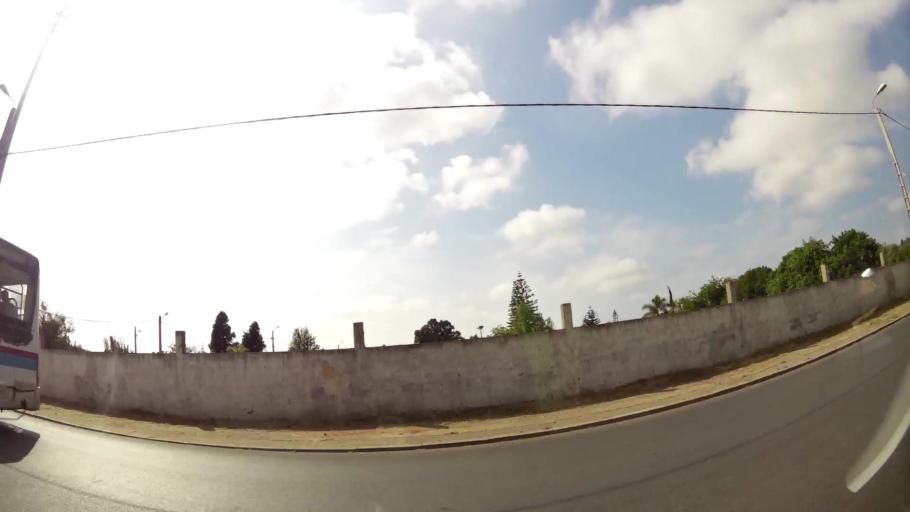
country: MA
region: Rabat-Sale-Zemmour-Zaer
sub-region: Rabat
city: Rabat
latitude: 33.9723
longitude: -6.8523
